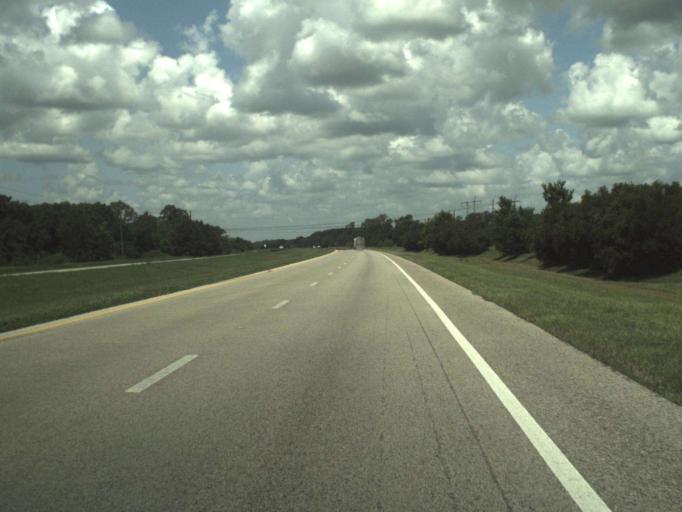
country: US
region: Florida
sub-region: Indian River County
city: Fellsmere
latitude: 27.6810
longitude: -80.8288
